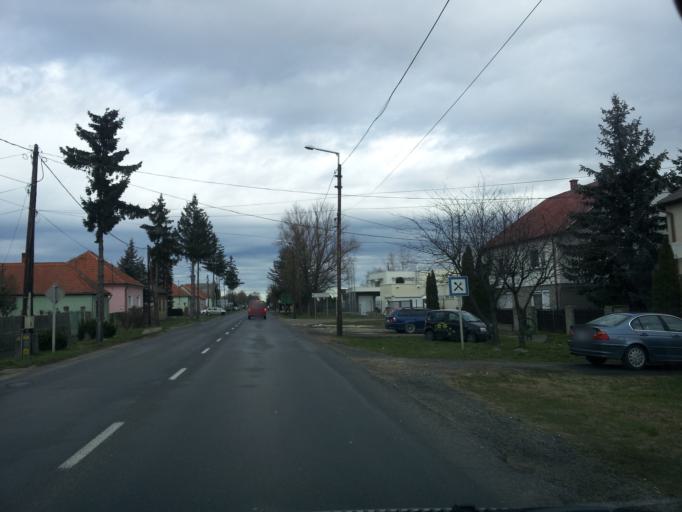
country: HU
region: Vas
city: Gencsapati
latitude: 47.3409
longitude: 16.5787
